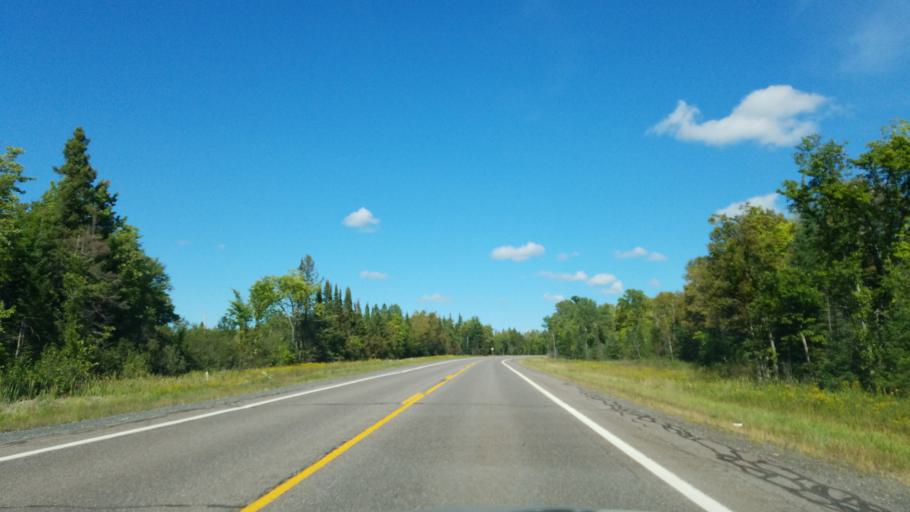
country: US
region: Michigan
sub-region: Baraga County
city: L'Anse
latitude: 46.5780
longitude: -88.4881
